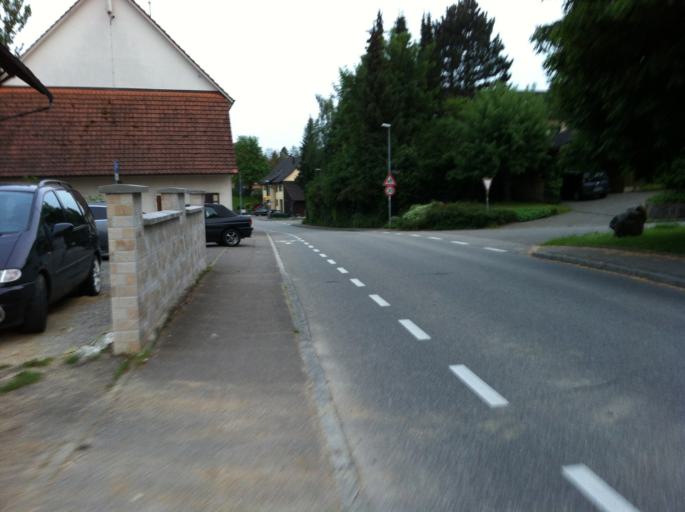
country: DE
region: Baden-Wuerttemberg
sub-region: Freiburg Region
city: Rheinfelden (Baden)
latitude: 47.6022
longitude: 7.7907
